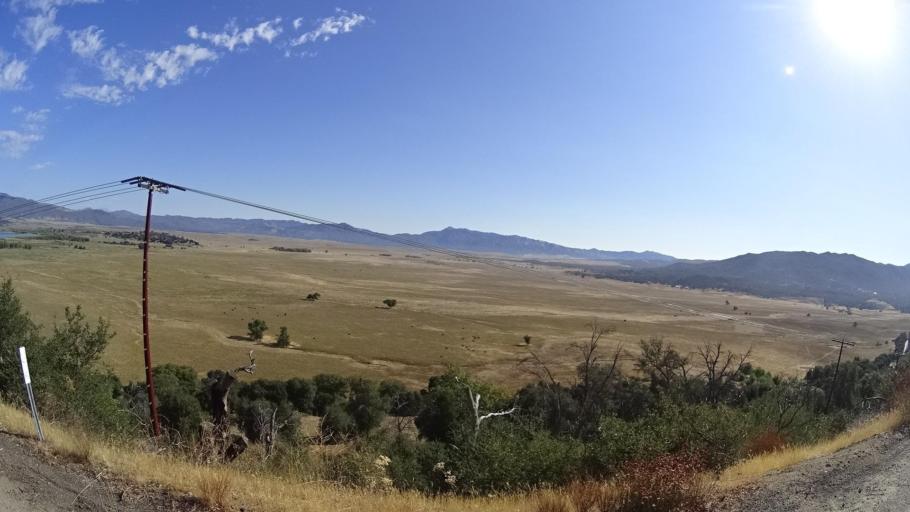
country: US
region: California
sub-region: San Diego County
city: Julian
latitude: 33.2098
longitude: -116.7347
